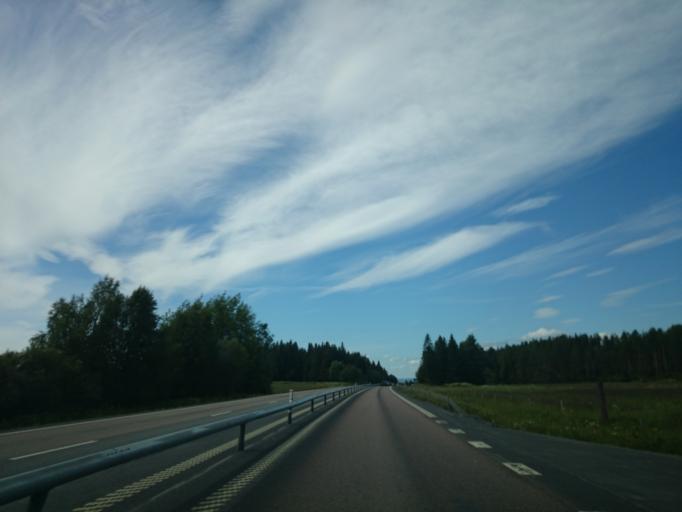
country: SE
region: Jaemtland
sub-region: Krokoms Kommun
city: Krokom
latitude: 63.2617
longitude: 14.5476
